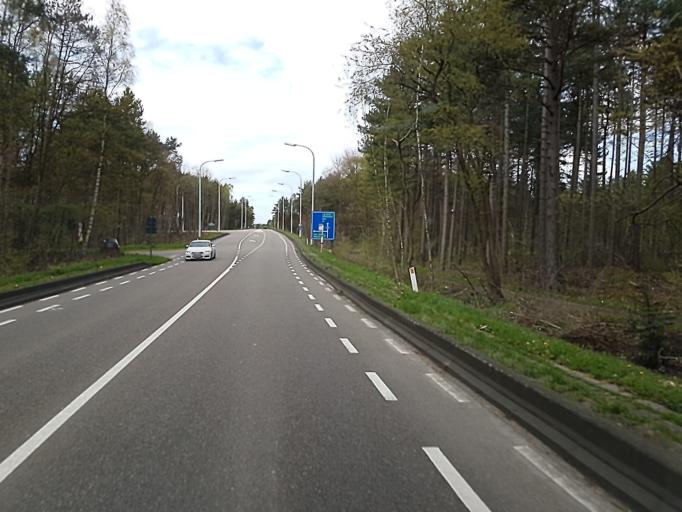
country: BE
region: Flanders
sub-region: Provincie Limburg
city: Zutendaal
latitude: 50.9730
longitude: 5.5524
